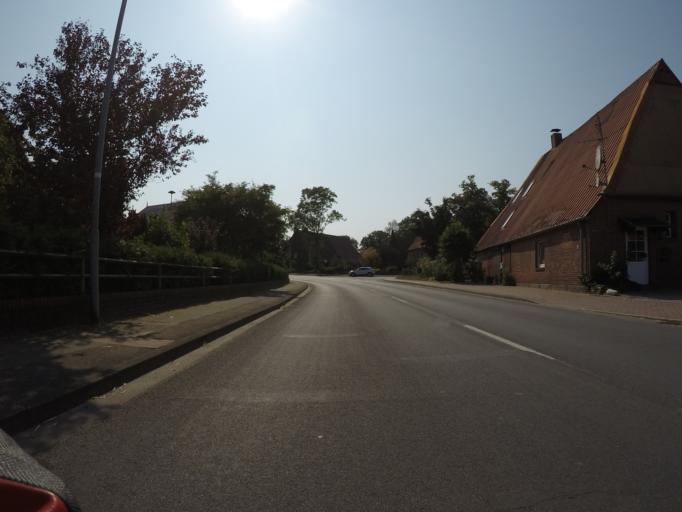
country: DE
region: Schleswig-Holstein
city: Bark
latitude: 53.9106
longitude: 10.1858
